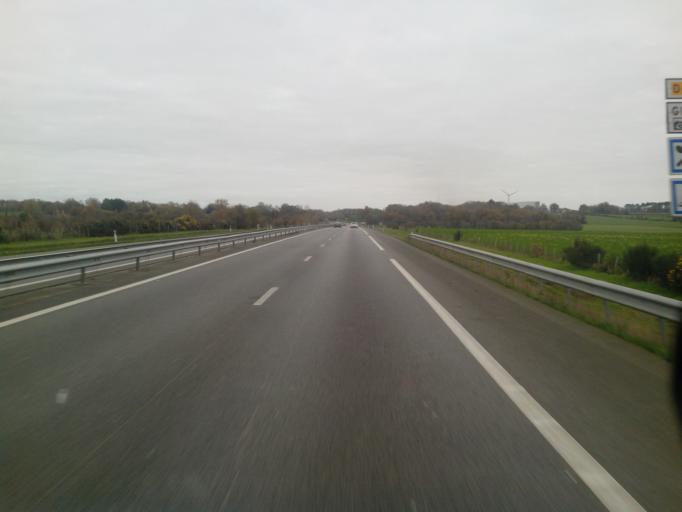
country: FR
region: Brittany
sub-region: Departement d'Ille-et-Vilaine
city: La Dominelais
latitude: 47.7617
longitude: -1.7118
